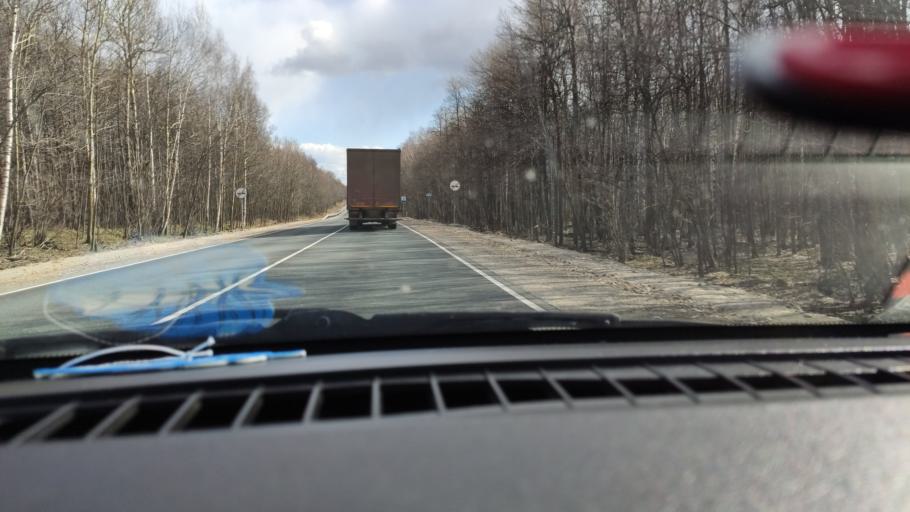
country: RU
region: Saratov
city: Khvalynsk
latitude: 52.4685
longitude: 48.0164
